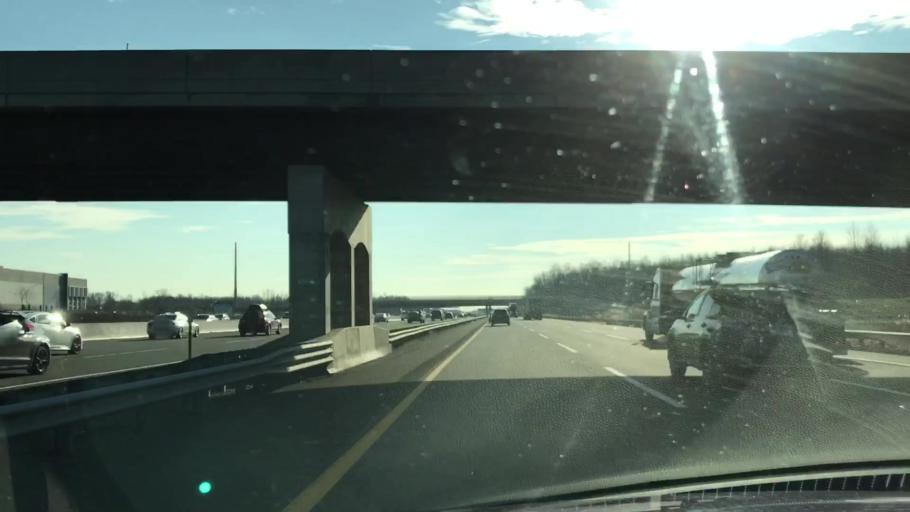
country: US
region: New Jersey
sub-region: Mercer County
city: Hightstown
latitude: 40.2793
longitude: -74.5053
